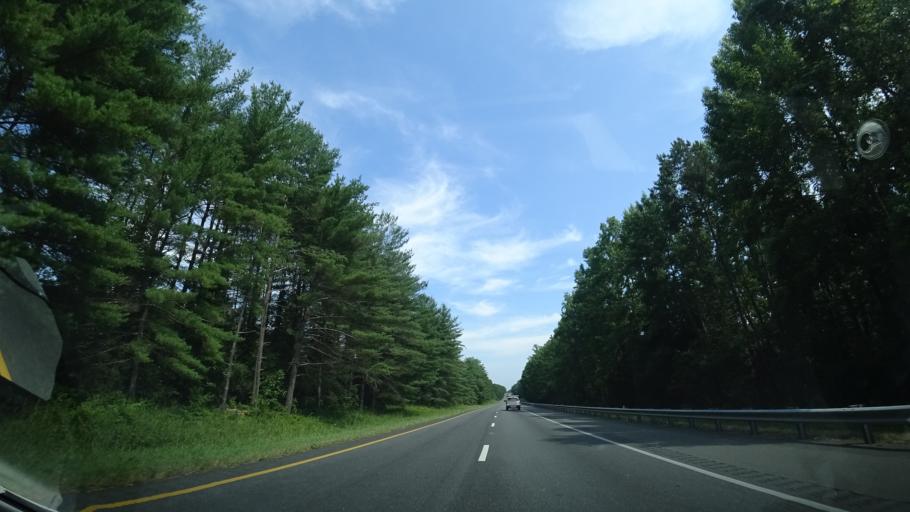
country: US
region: Virginia
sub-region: Louisa County
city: Louisa
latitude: 37.9277
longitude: -78.0866
